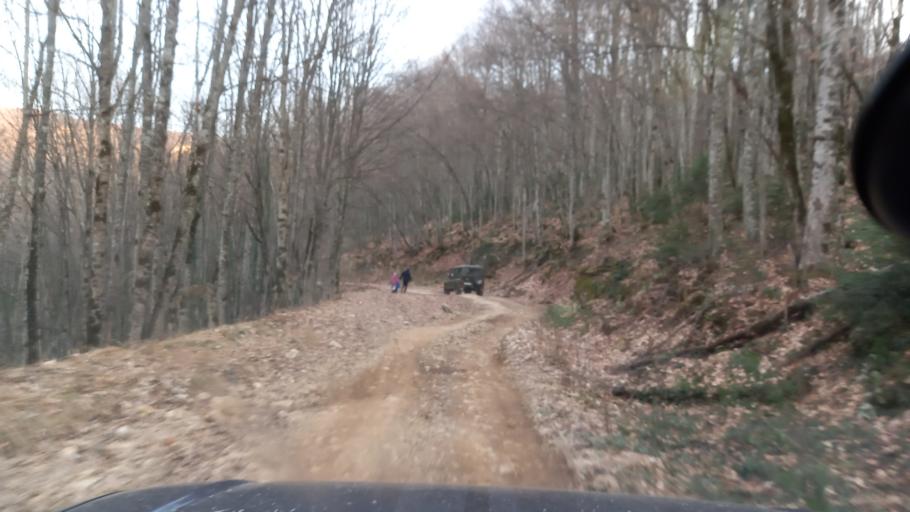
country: RU
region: Krasnodarskiy
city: Neftegorsk
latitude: 44.2165
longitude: 39.8997
